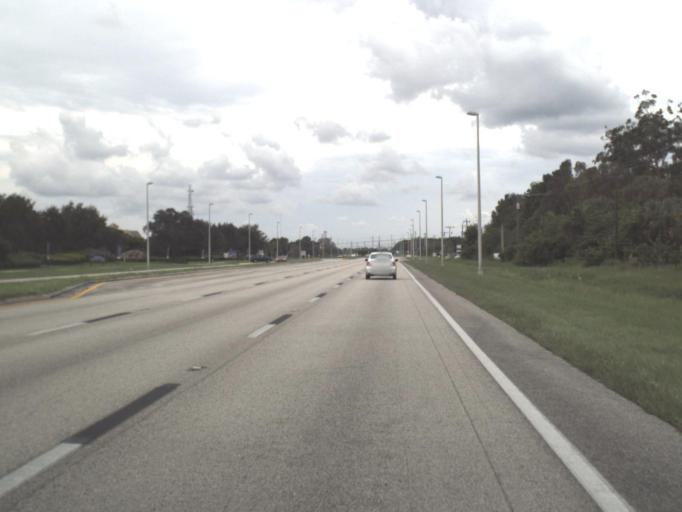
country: US
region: Florida
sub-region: Lee County
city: Fort Myers Shores
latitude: 26.7001
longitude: -81.7652
